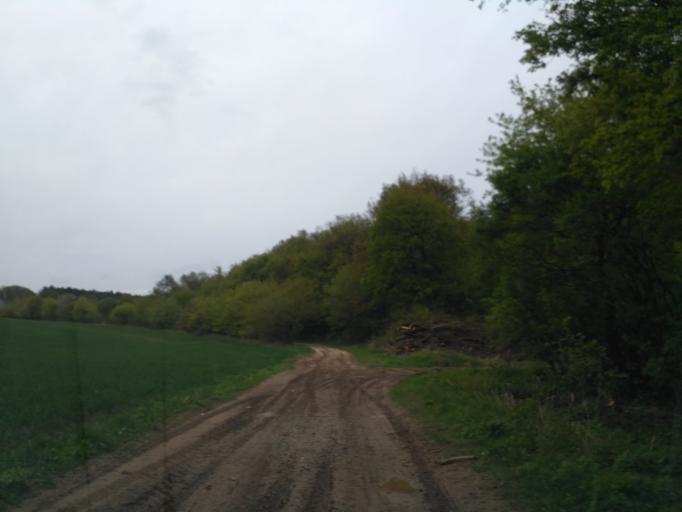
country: SK
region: Kosicky
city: Moldava nad Bodvou
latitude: 48.6573
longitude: 21.0036
